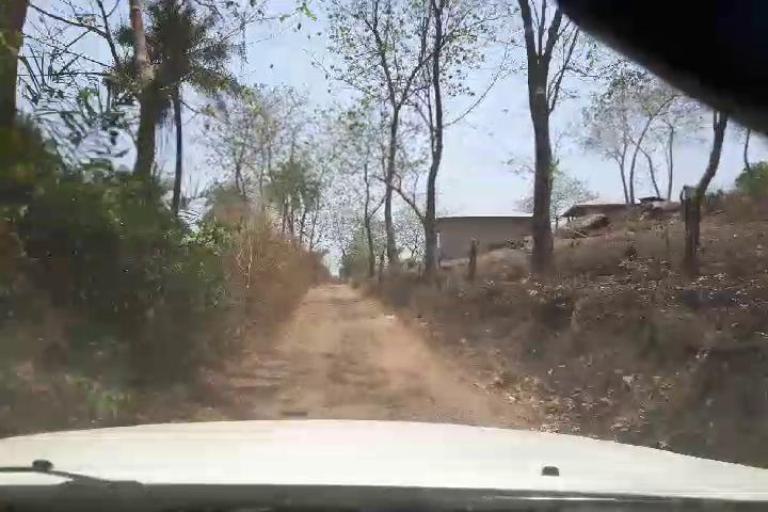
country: SL
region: Northern Province
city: Alikalia
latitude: 9.0684
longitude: -11.4835
